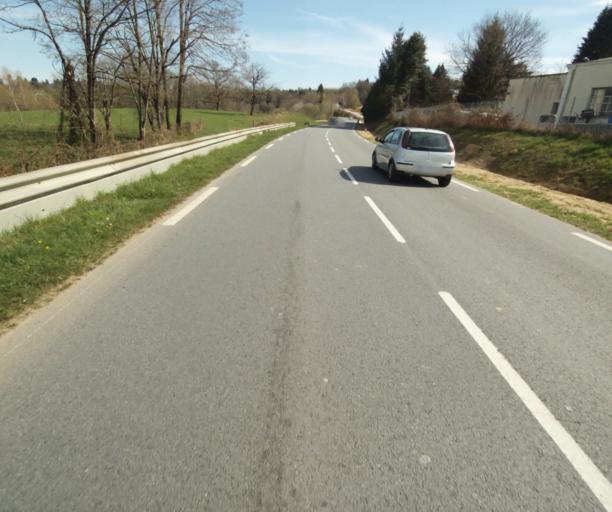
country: FR
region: Limousin
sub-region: Departement de la Correze
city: Naves
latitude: 45.3366
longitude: 1.7503
